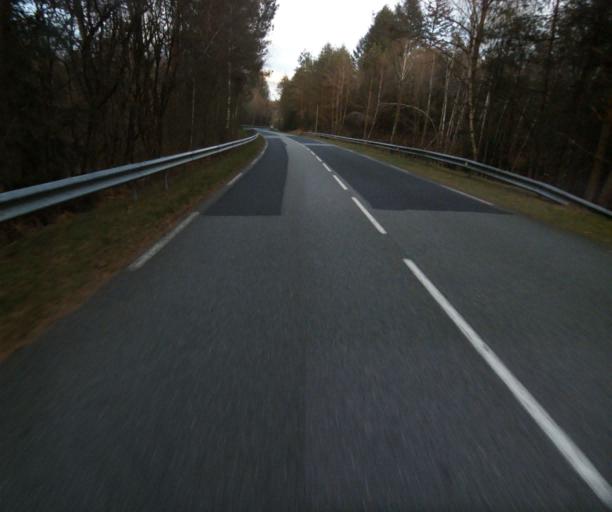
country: FR
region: Limousin
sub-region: Departement de la Correze
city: Correze
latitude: 45.2807
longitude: 1.9269
